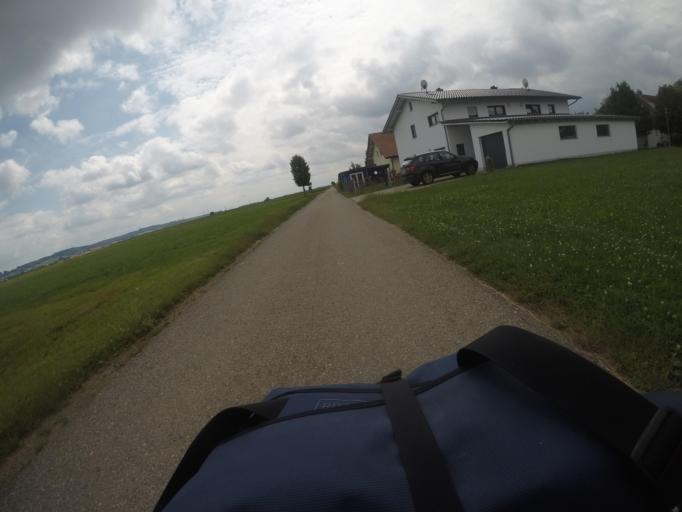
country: DE
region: Bavaria
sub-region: Swabia
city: Fellheim
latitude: 48.0691
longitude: 10.1564
